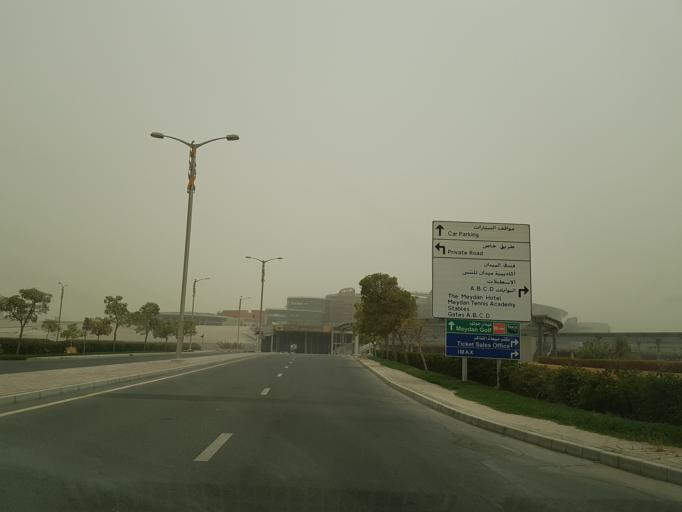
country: AE
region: Dubai
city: Dubai
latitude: 25.1635
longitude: 55.3033
